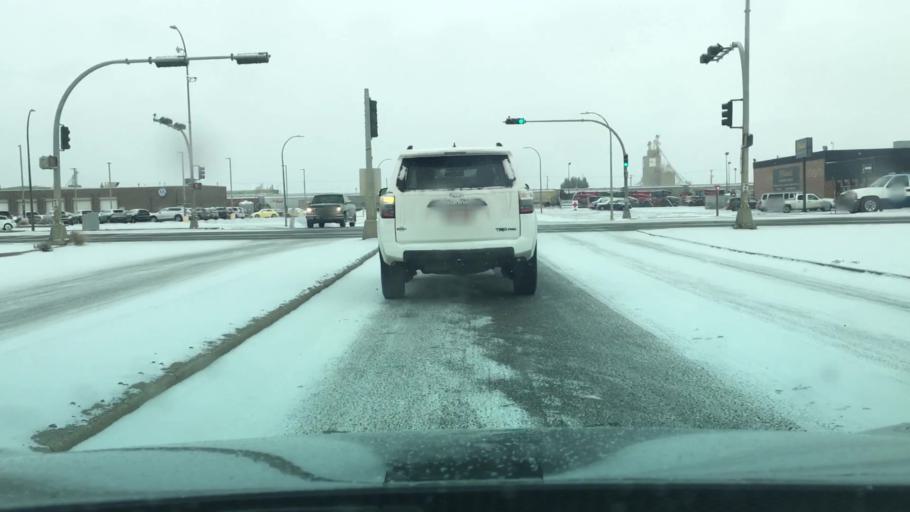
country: CA
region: Alberta
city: Lethbridge
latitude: 49.6978
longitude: -112.7877
